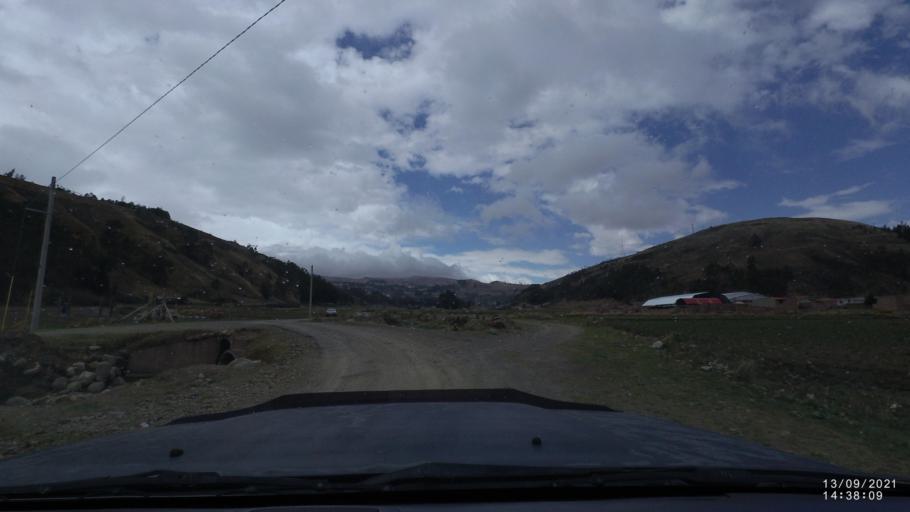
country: BO
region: Cochabamba
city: Colomi
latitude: -17.3702
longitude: -65.8331
